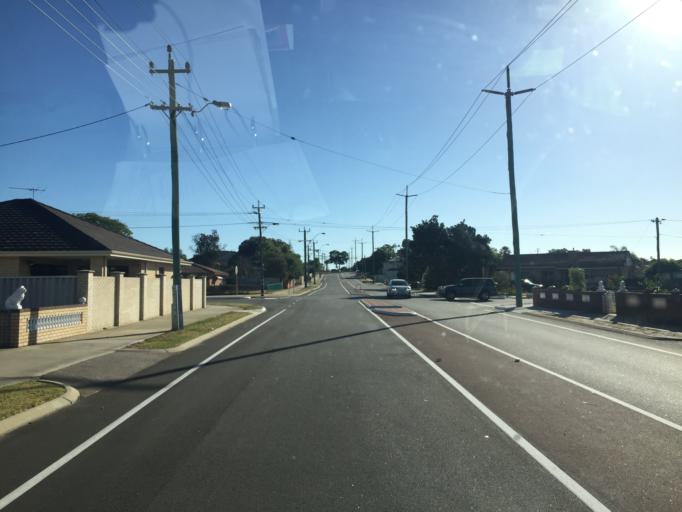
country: AU
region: Western Australia
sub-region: Belmont
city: Rivervale
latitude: -31.9659
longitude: 115.9227
